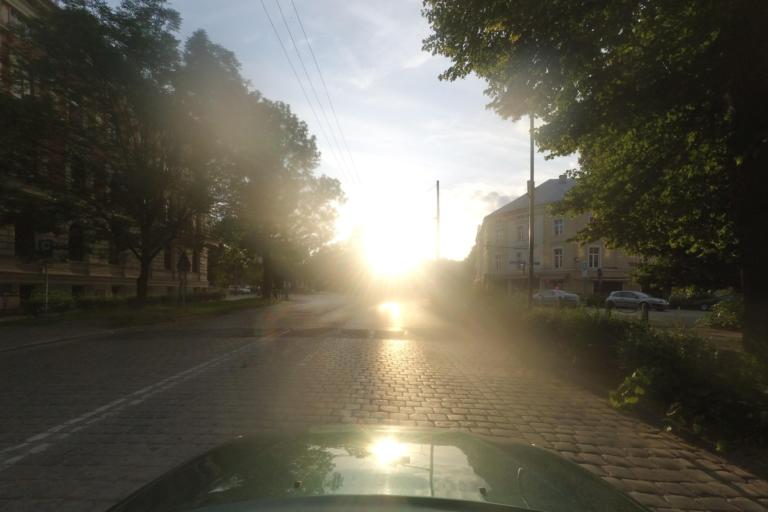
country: PL
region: Lower Silesian Voivodeship
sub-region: Powiat swidnicki
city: Swidnica
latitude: 50.8408
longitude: 16.4850
